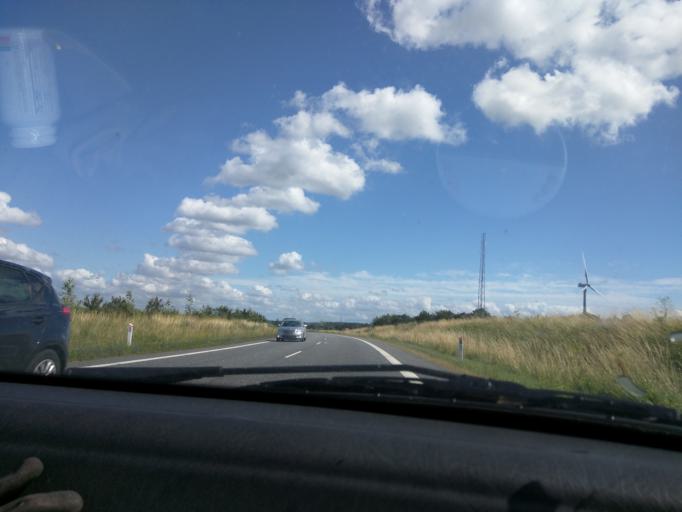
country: DK
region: Zealand
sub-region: Kalundborg Kommune
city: Svebolle
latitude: 55.6705
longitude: 11.2122
